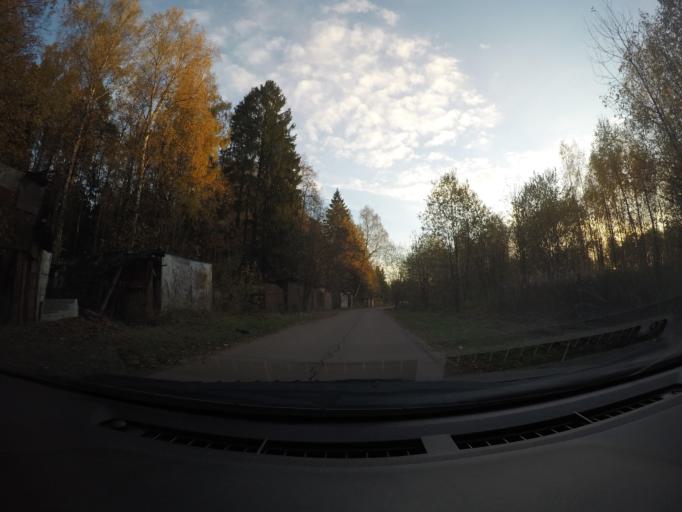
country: RU
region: Moskovskaya
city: Firsanovka
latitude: 55.9268
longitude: 37.2360
